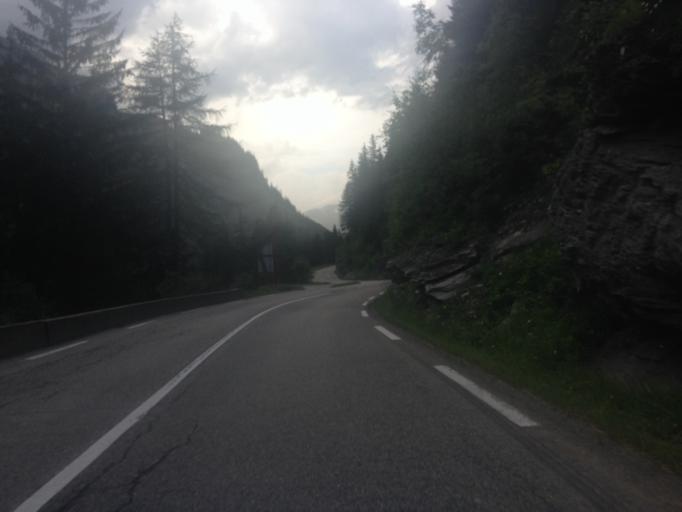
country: FR
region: Rhone-Alpes
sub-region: Departement de la Savoie
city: Tignes
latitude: 45.5222
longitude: 6.9140
